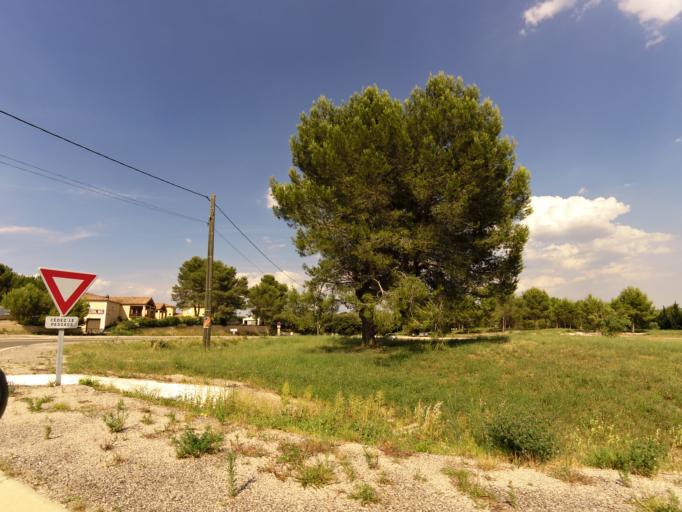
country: FR
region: Languedoc-Roussillon
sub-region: Departement du Gard
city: Sommieres
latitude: 43.8129
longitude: 4.0604
